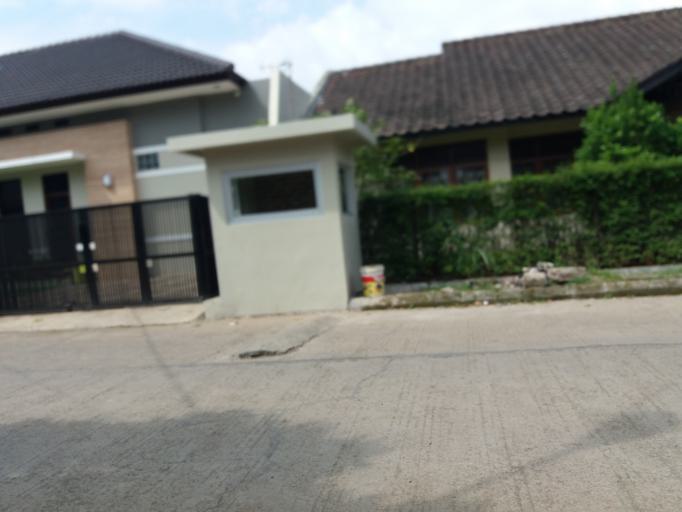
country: ID
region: West Java
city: Bandung
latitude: -6.9162
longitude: 107.6521
